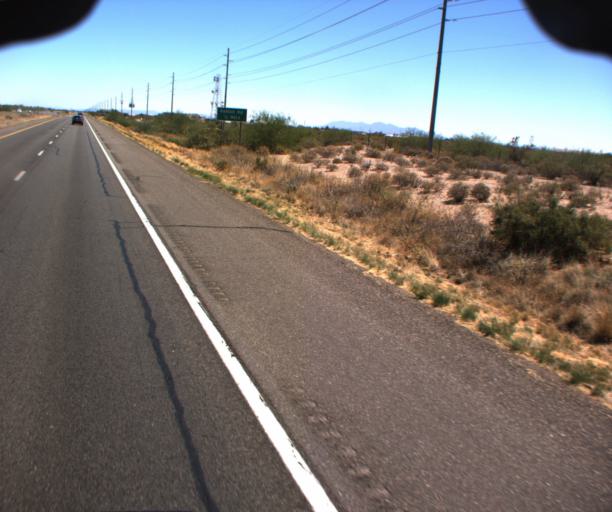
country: US
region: Arizona
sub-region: Maricopa County
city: Sun City West
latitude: 33.7432
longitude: -112.4844
